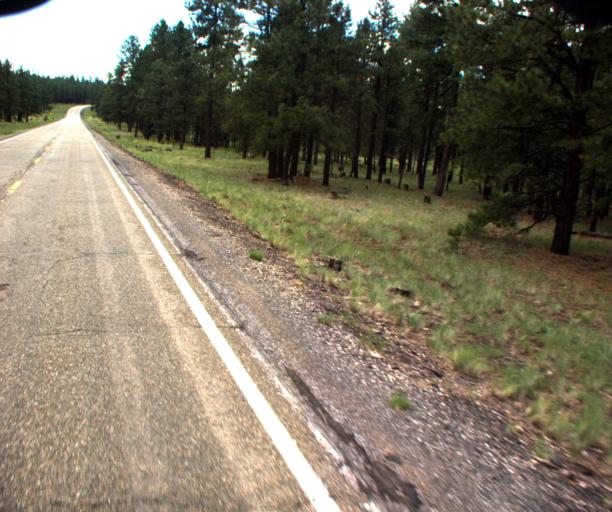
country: US
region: Arizona
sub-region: Coconino County
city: Parks
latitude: 35.3611
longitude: -111.7912
